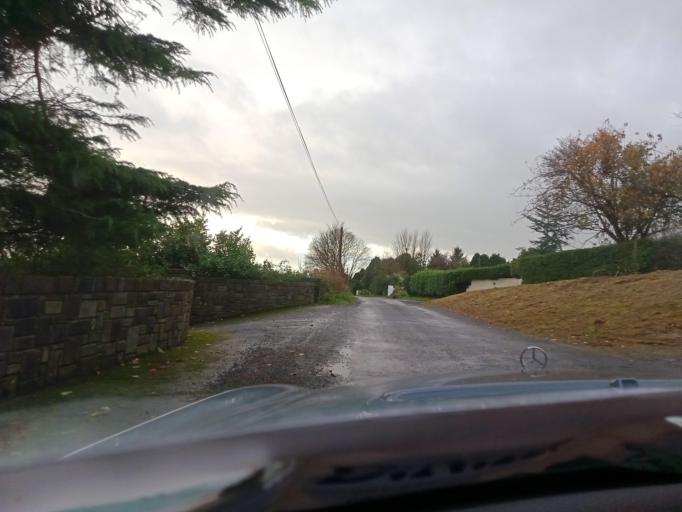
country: IE
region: Leinster
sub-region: Kilkenny
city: Mooncoin
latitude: 52.2707
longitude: -7.1852
